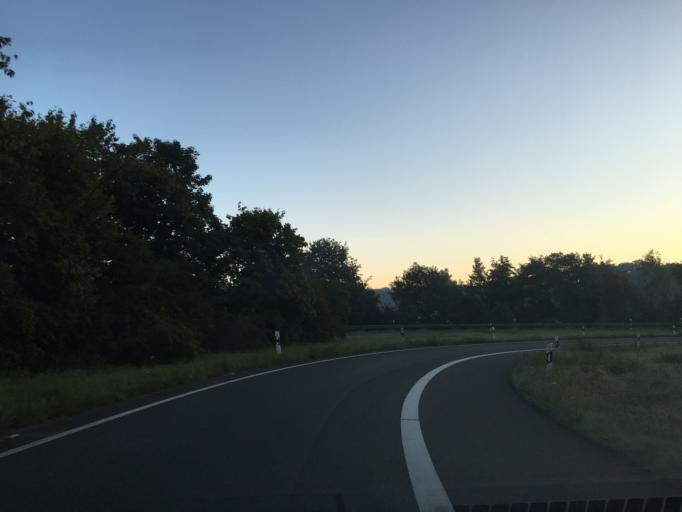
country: DE
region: North Rhine-Westphalia
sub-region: Regierungsbezirk Munster
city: Steinfurt
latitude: 52.1399
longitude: 7.3660
